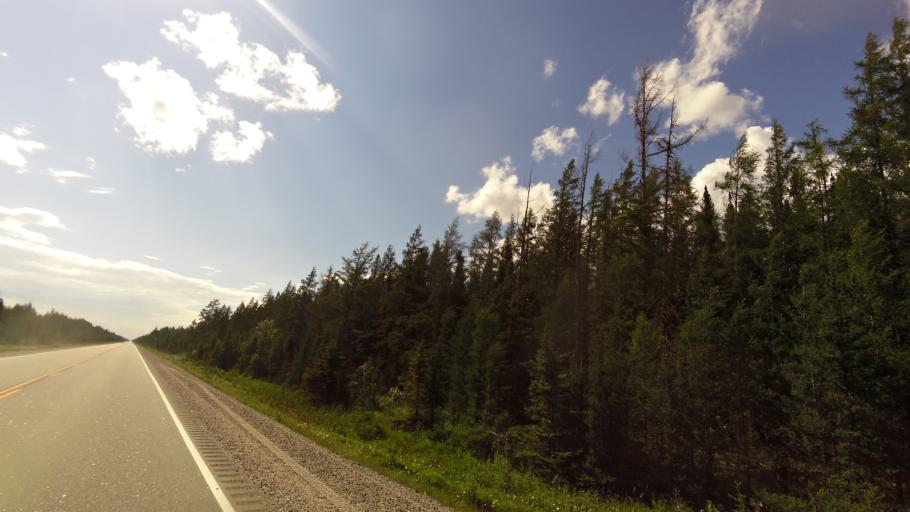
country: CA
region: Ontario
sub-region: Algoma
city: Hornepayne
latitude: 49.7728
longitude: -84.7035
